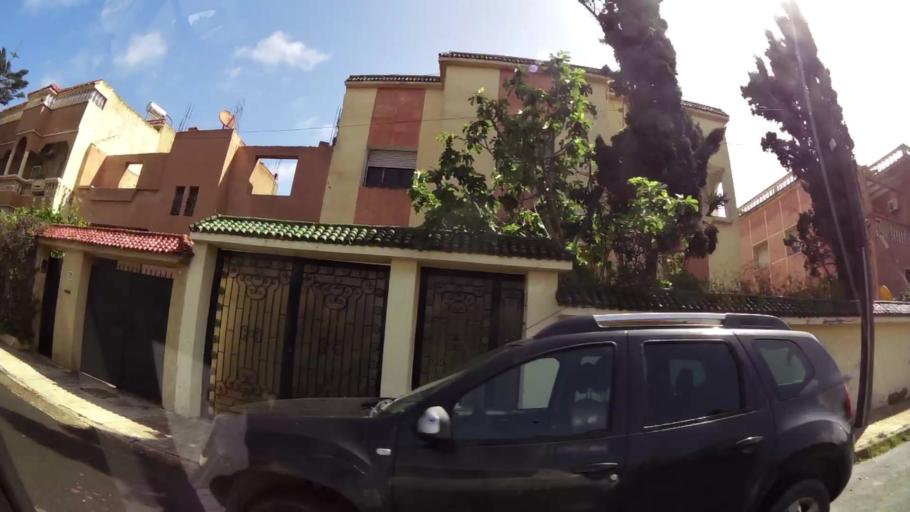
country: MA
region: Grand Casablanca
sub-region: Mediouna
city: Tit Mellil
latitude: 33.6181
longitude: -7.5229
